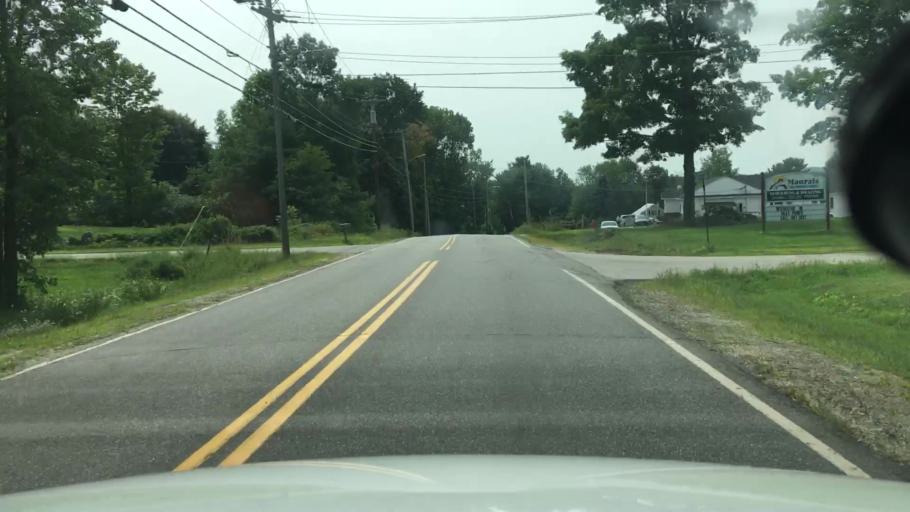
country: US
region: Maine
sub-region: Androscoggin County
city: Livermore Falls
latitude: 44.4826
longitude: -70.1865
